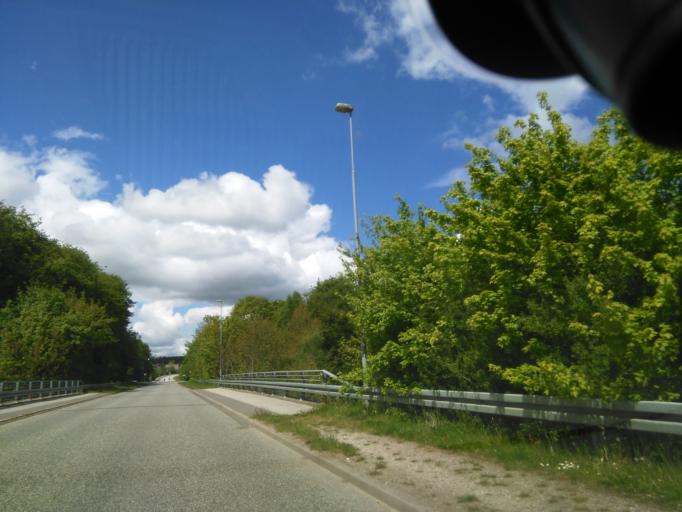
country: DK
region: Central Jutland
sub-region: Skanderborg Kommune
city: Horning
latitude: 56.0774
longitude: 10.0278
